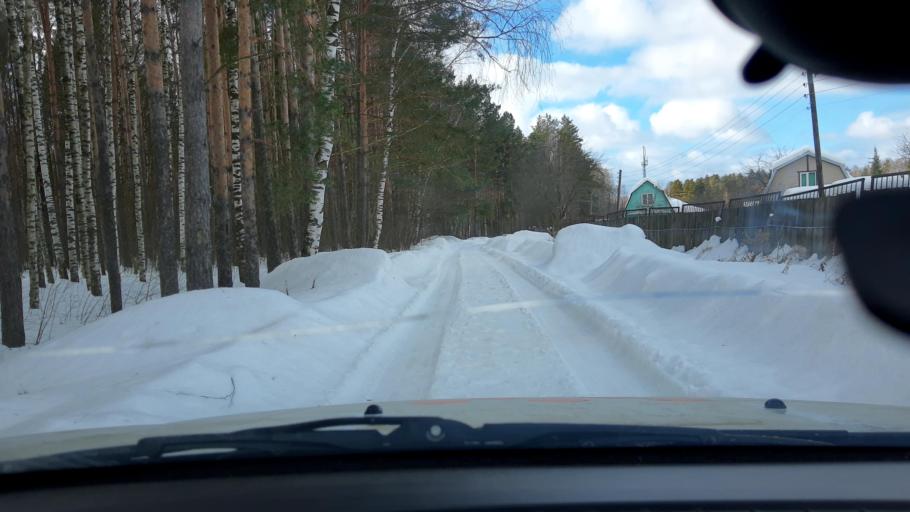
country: RU
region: Nizjnij Novgorod
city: Neklyudovo
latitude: 56.4500
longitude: 43.9885
